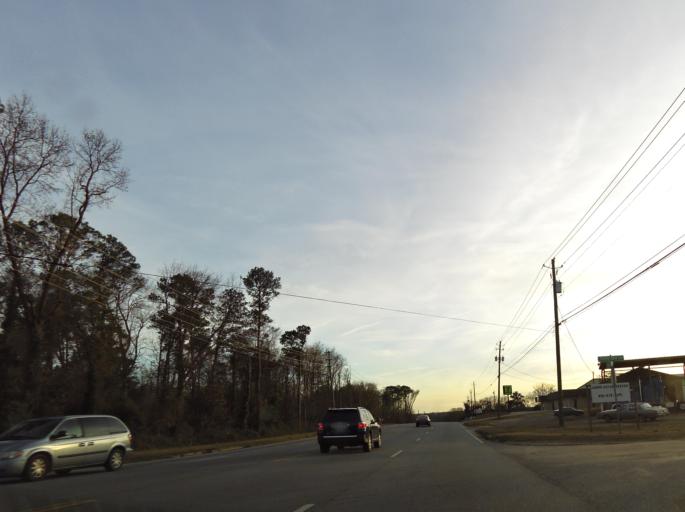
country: US
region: Georgia
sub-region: Bibb County
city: Macon
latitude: 32.7783
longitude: -83.6562
